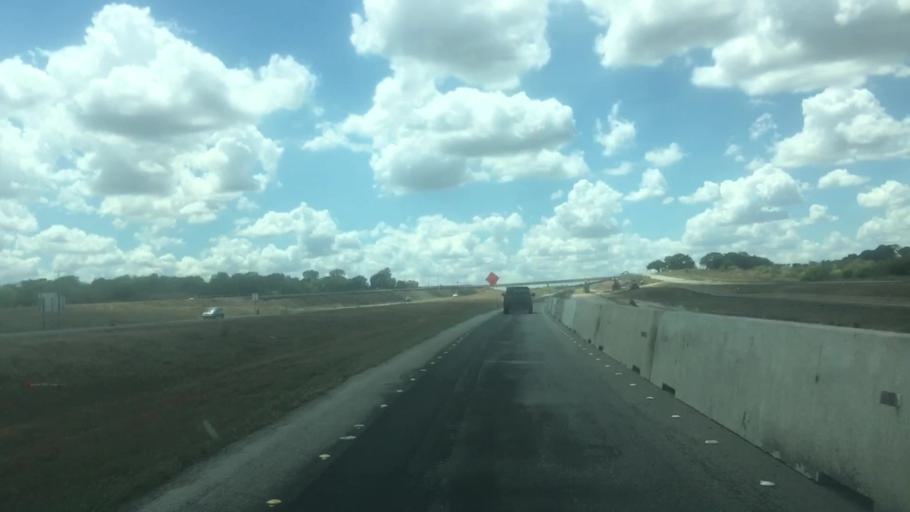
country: US
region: Texas
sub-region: Caldwell County
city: Lockhart
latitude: 29.8570
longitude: -97.7132
